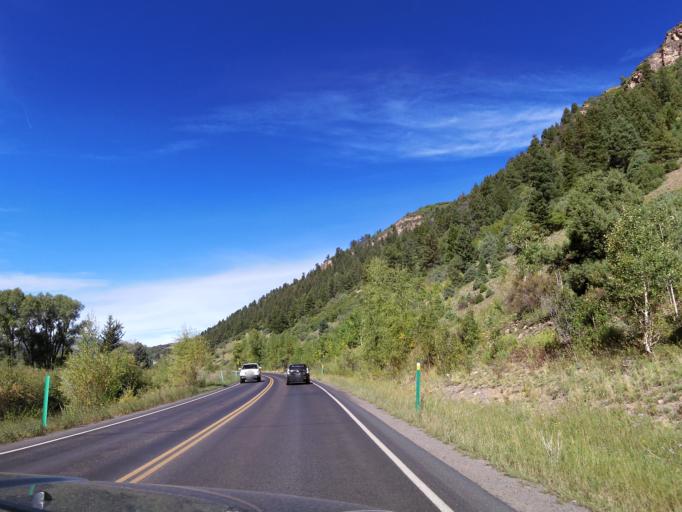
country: US
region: Colorado
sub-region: San Miguel County
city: Mountain Village
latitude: 37.9513
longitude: -107.8572
